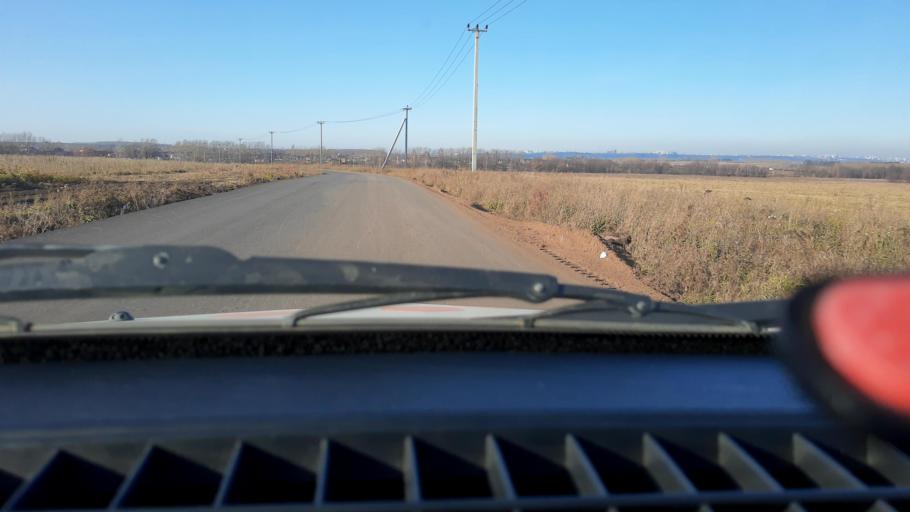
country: RU
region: Bashkortostan
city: Kabakovo
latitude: 54.6225
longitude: 56.1528
